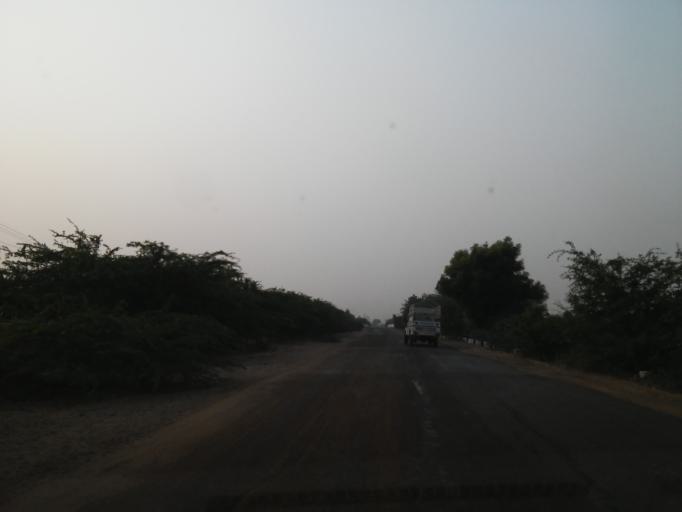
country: IN
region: Gujarat
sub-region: Kachchh
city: Bhuj
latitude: 23.8655
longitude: 69.7277
